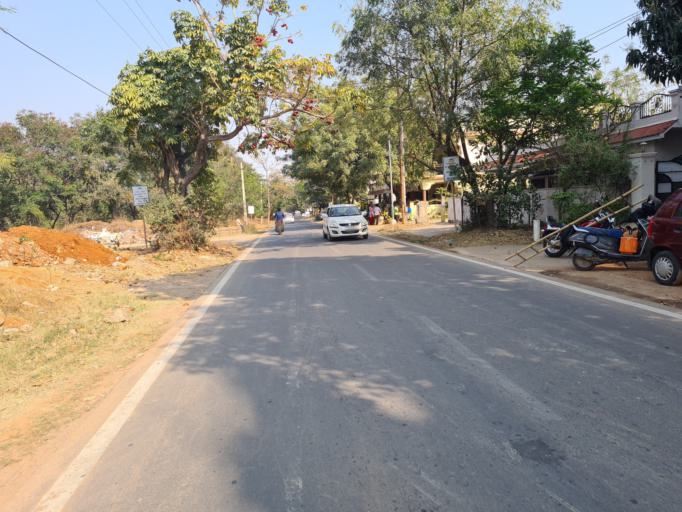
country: IN
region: Telangana
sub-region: Medak
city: Serilingampalle
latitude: 17.4853
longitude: 78.3070
